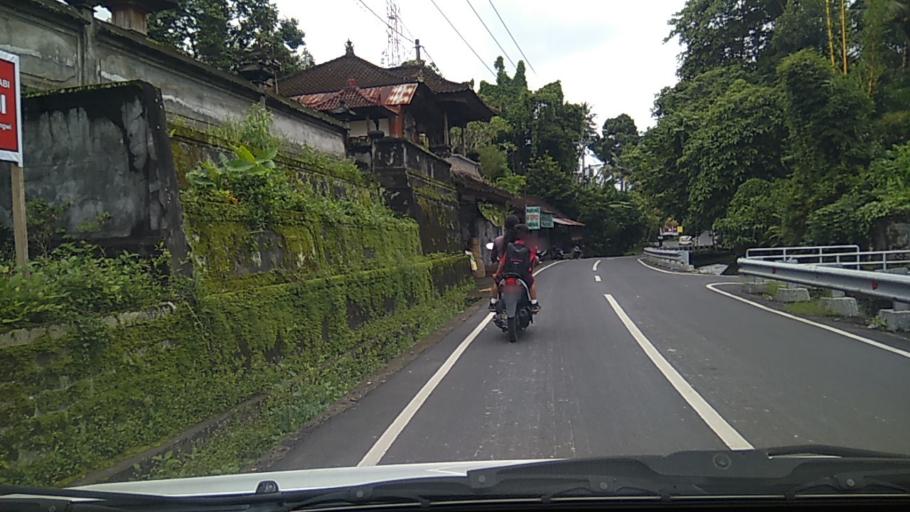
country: ID
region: Bali
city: Basa
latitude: -8.4727
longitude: 115.1853
